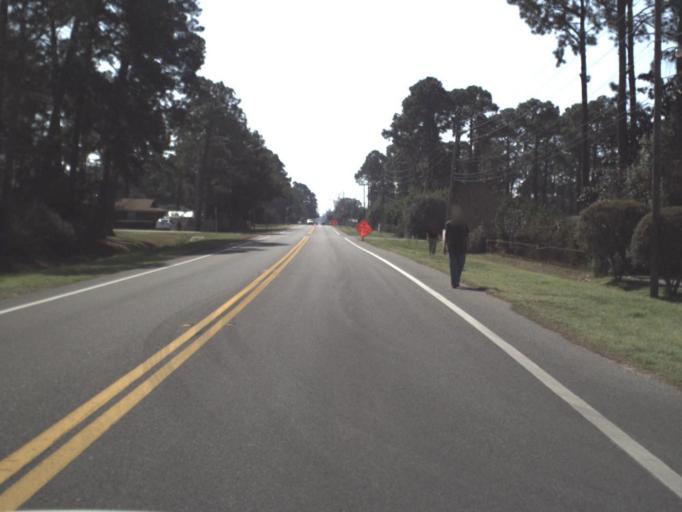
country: US
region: Florida
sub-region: Bay County
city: Pretty Bayou
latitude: 30.1878
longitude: -85.7012
